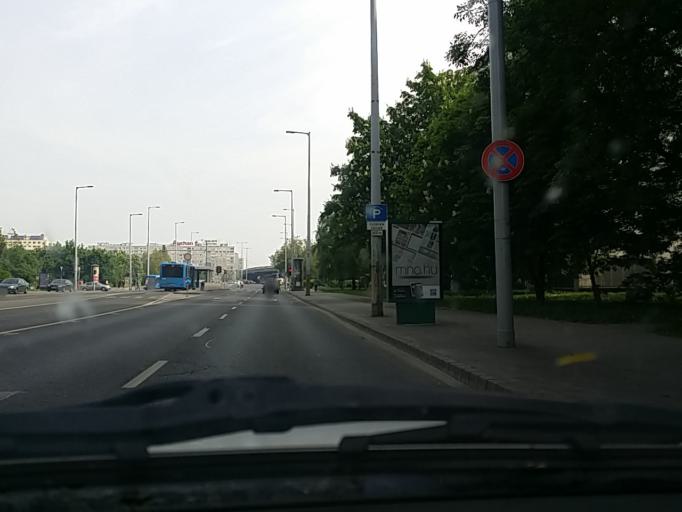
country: HU
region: Budapest
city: Budapest III. keruelet
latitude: 47.5381
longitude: 19.0404
